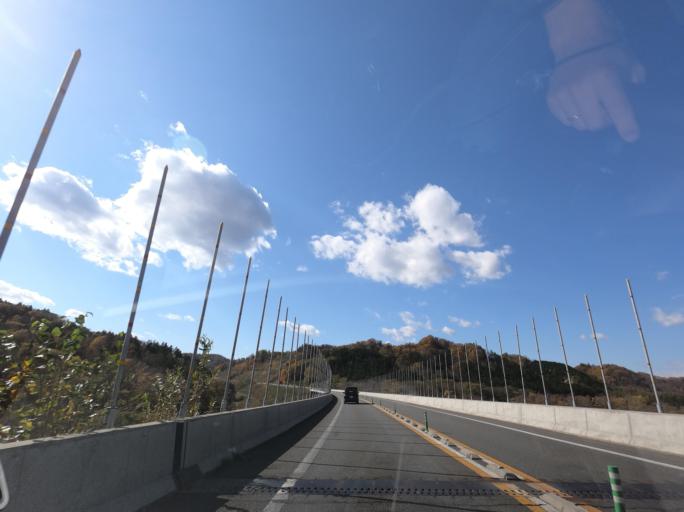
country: JP
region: Hokkaido
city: Kushiro
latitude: 43.0883
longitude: 143.9207
